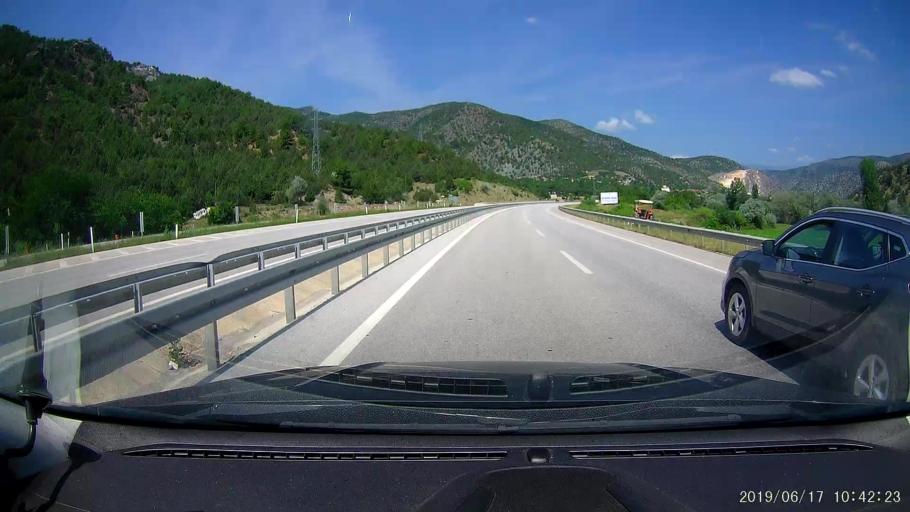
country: TR
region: Corum
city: Hacihamza
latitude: 41.0474
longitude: 34.5550
